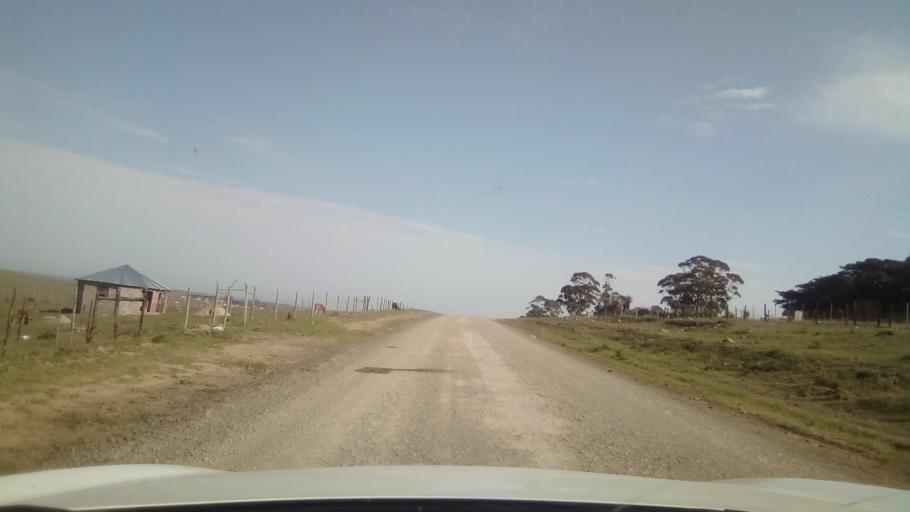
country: ZA
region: Eastern Cape
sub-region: Buffalo City Metropolitan Municipality
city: Bhisho
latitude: -32.9861
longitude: 27.2605
